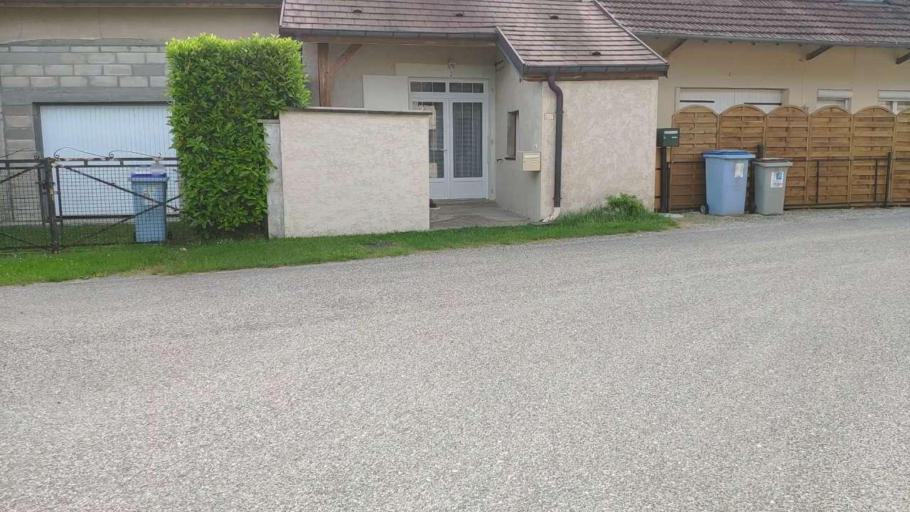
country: FR
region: Franche-Comte
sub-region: Departement du Jura
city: Bletterans
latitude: 46.7366
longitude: 5.4614
